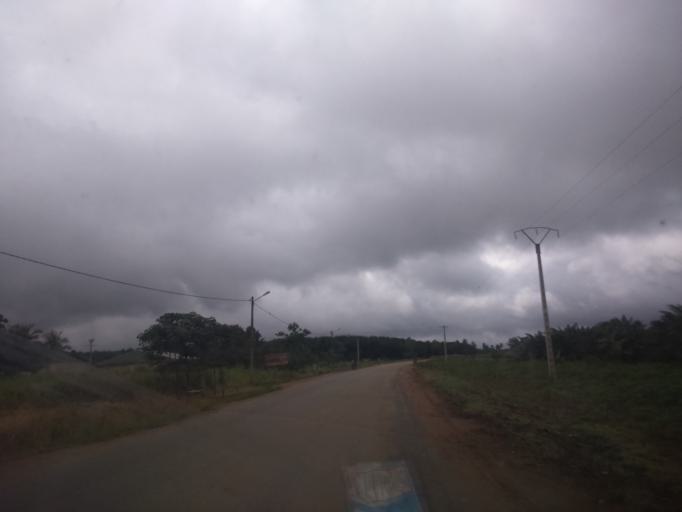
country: CI
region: Sud-Comoe
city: Adiake
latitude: 5.2969
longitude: -3.4359
